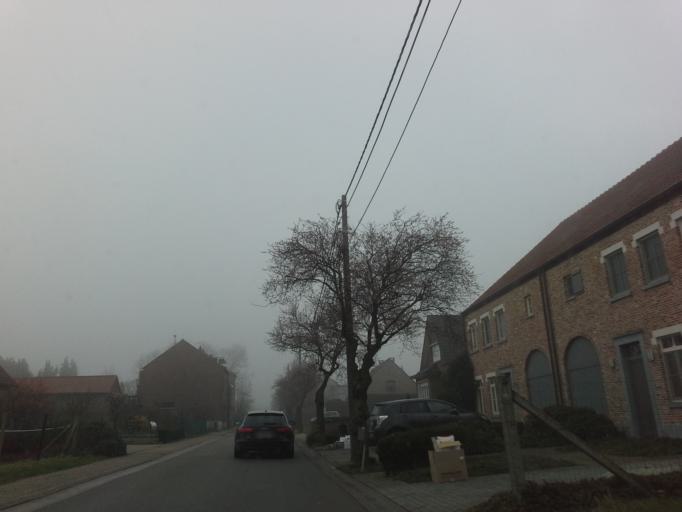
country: BE
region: Flanders
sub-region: Provincie Vlaams-Brabant
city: Holsbeek
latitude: 50.8755
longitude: 4.7622
